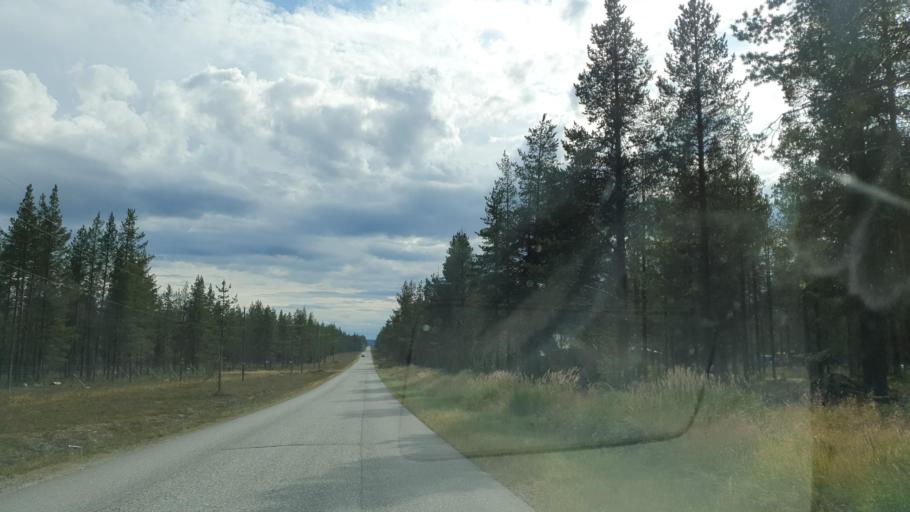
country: FI
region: Lapland
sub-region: Tunturi-Lappi
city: Kolari
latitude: 67.6539
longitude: 24.1633
